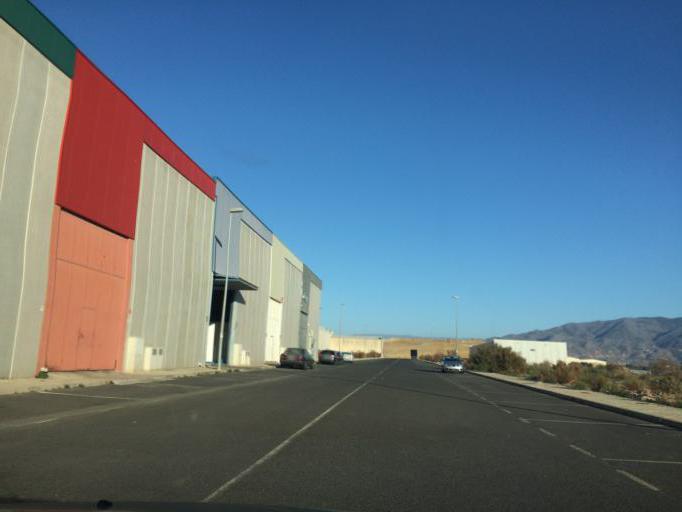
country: ES
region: Andalusia
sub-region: Provincia de Almeria
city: Viator
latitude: 36.8759
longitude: -2.4118
